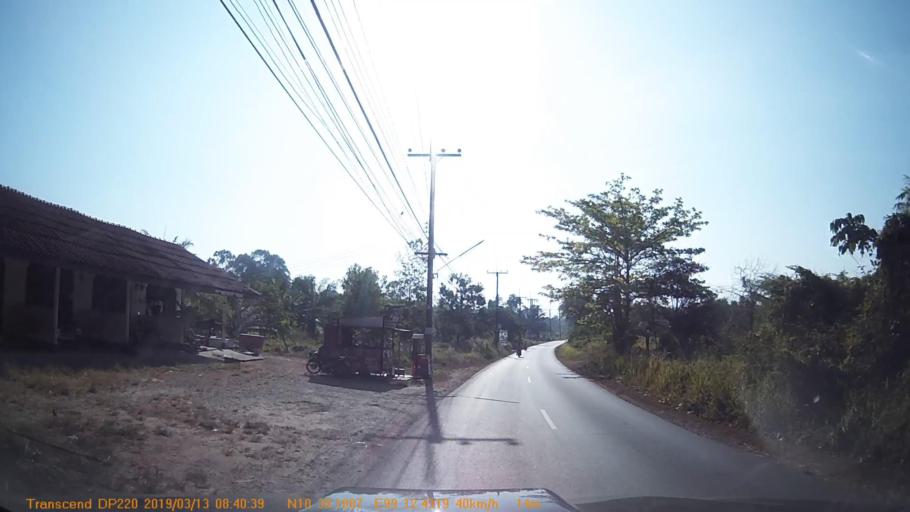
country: TH
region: Chumphon
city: Chumphon
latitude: 10.5018
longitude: 99.2074
